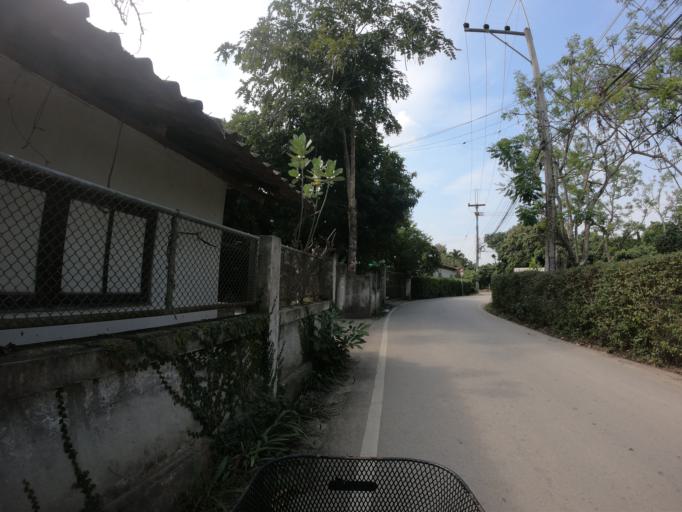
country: TH
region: Chiang Mai
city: Saraphi
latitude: 18.7102
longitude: 99.0200
